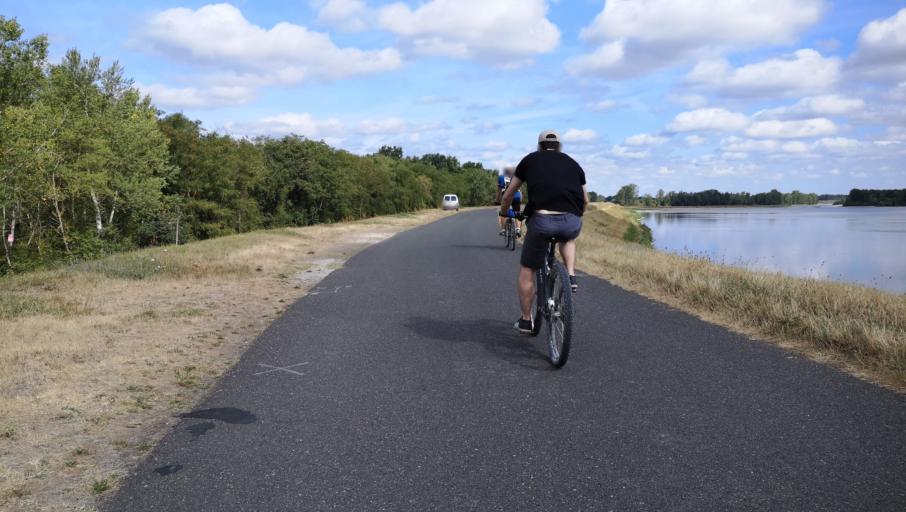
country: FR
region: Centre
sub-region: Departement du Loiret
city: Sandillon
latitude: 47.8575
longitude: 2.0312
